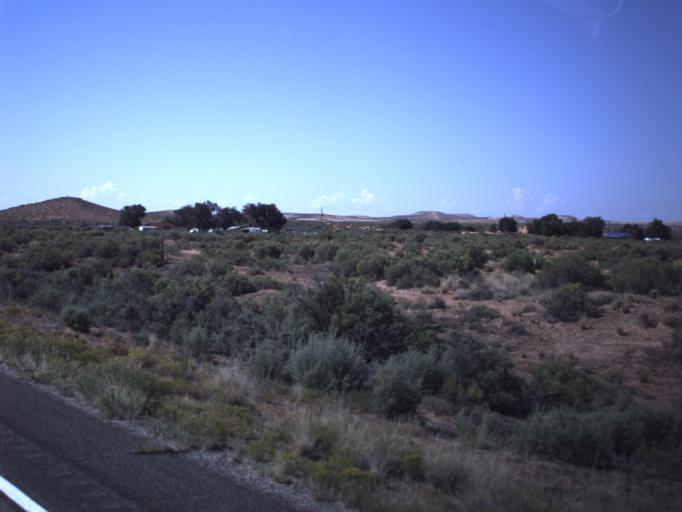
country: US
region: Utah
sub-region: San Juan County
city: Blanding
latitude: 37.1064
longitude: -109.5465
